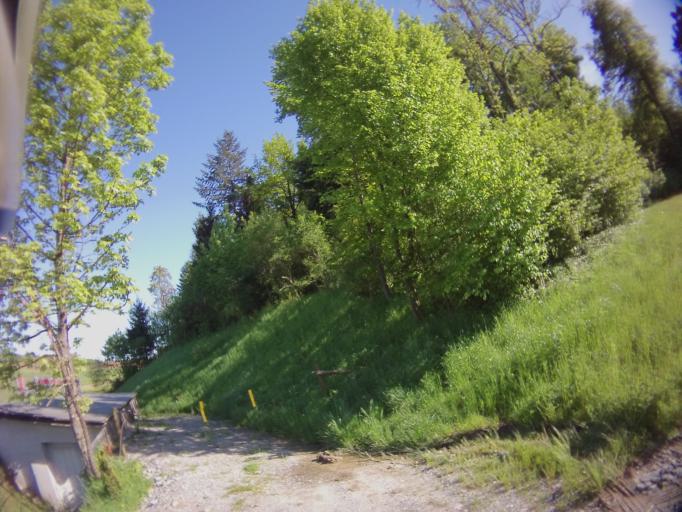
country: CH
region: Zurich
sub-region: Bezirk Affoltern
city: Knonau
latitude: 47.2089
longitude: 8.4435
